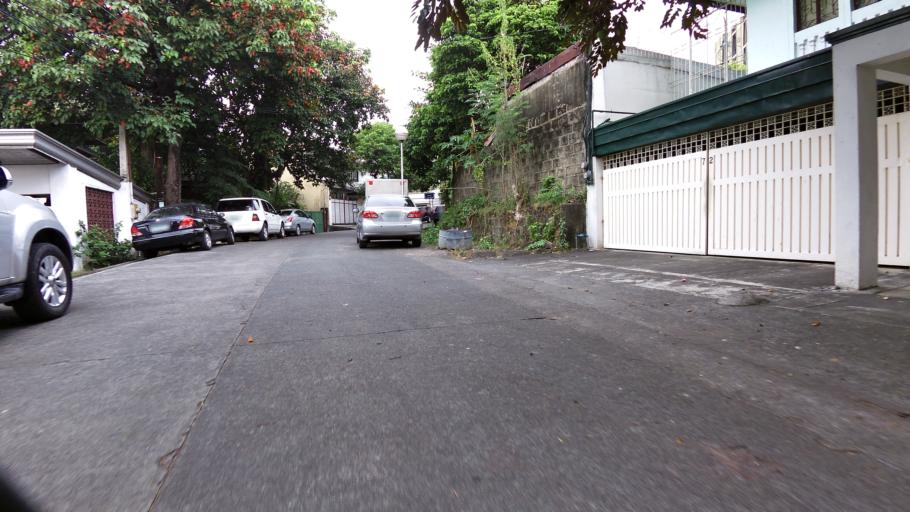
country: PH
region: Metro Manila
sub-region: Pasig
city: Pasig City
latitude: 14.5676
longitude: 121.0605
